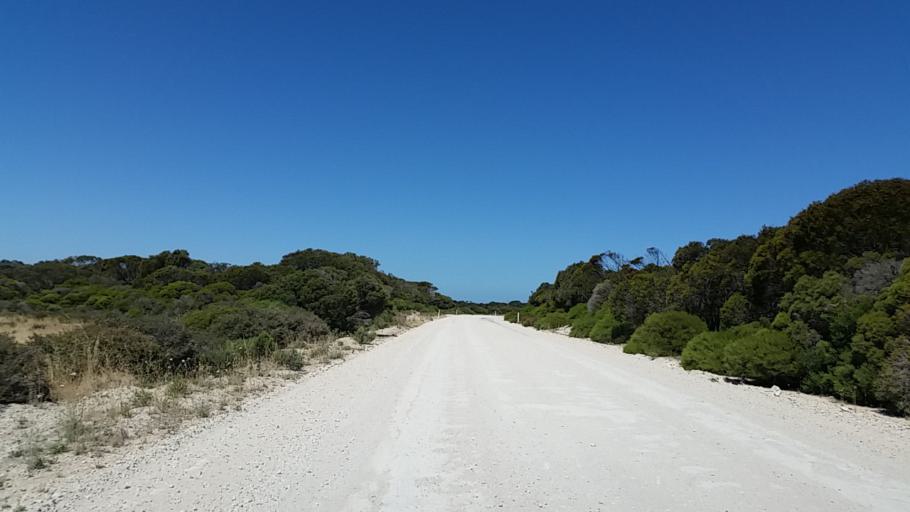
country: AU
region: South Australia
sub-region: Yorke Peninsula
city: Honiton
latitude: -35.2135
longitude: 137.0358
